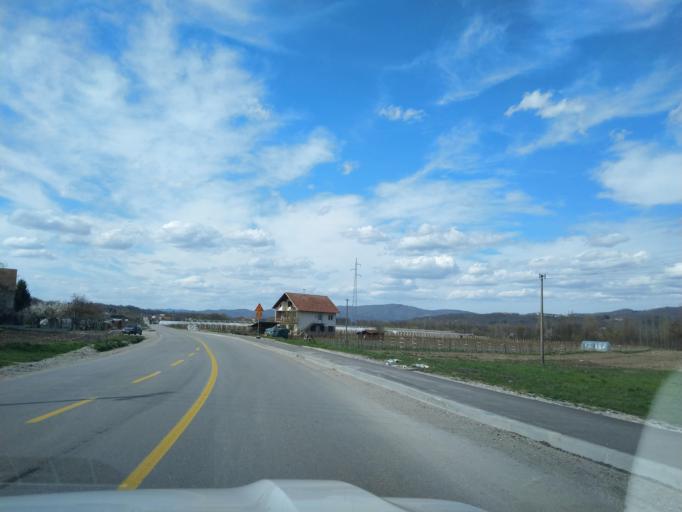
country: RS
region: Central Serbia
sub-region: Zlatiborski Okrug
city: Arilje
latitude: 43.7857
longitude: 20.1087
